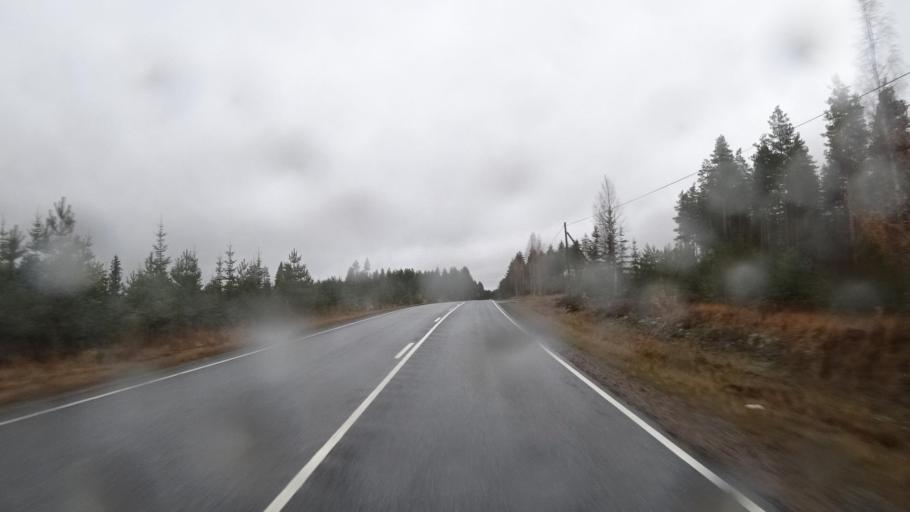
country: FI
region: Northern Savo
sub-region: Koillis-Savo
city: Tuusniemi
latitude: 62.8674
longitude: 28.3683
